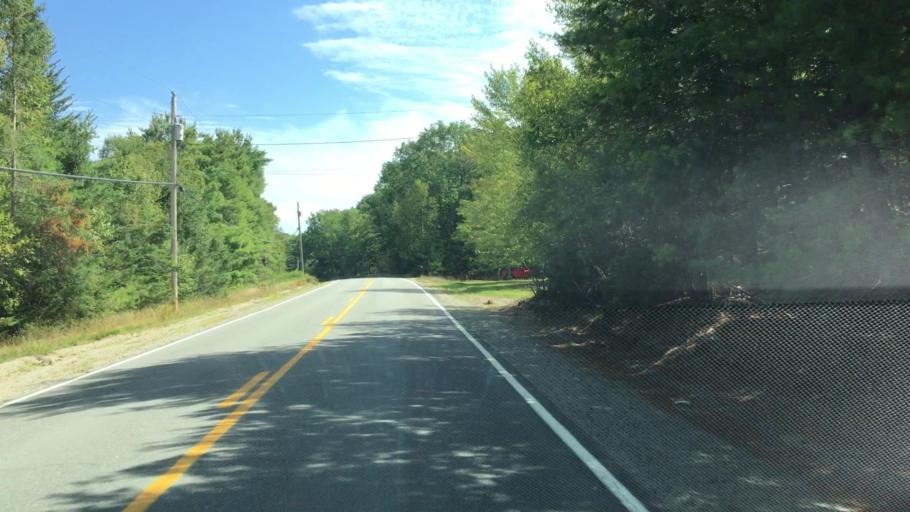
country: US
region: Maine
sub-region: Penobscot County
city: Holden
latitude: 44.7940
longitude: -68.5254
